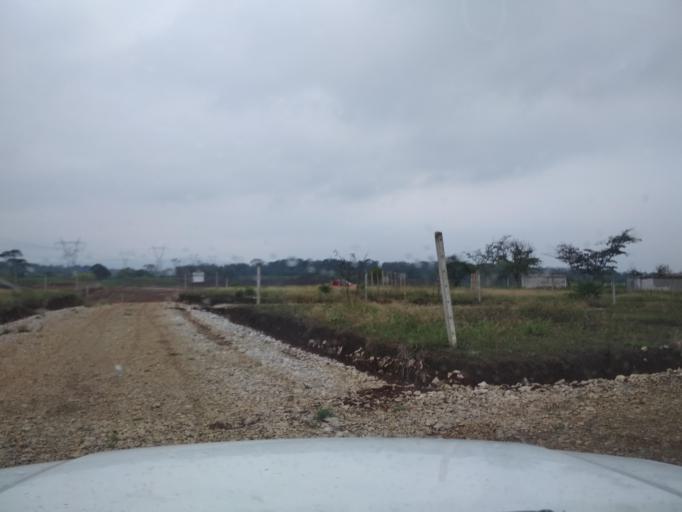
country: MX
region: Veracruz
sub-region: Cordoba
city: Fredepo
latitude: 18.8701
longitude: -96.9705
